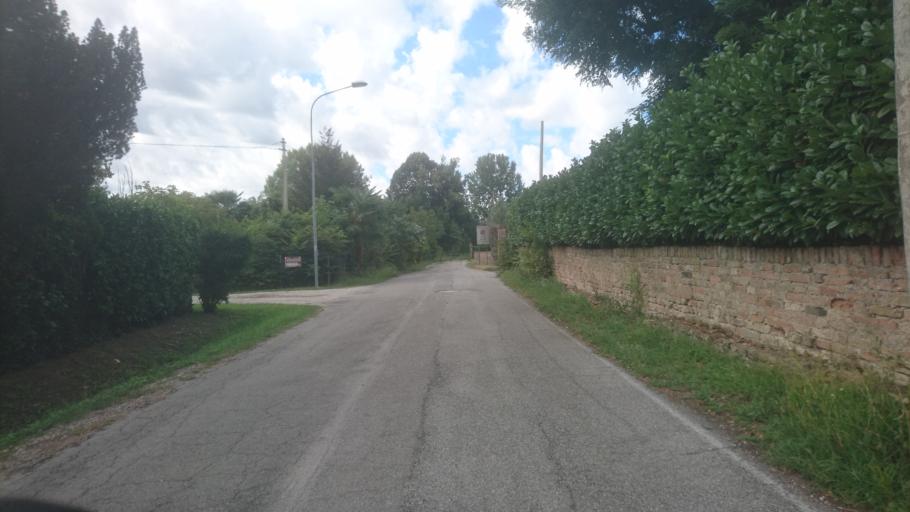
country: IT
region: Veneto
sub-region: Provincia di Venezia
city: Vigonovo
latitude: 45.3938
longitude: 12.0004
